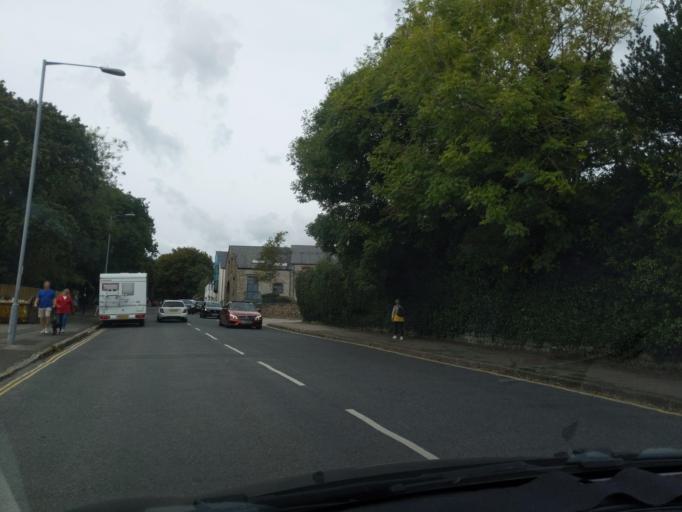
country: GB
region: England
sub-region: Cornwall
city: St Austell
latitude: 50.3357
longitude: -4.7623
